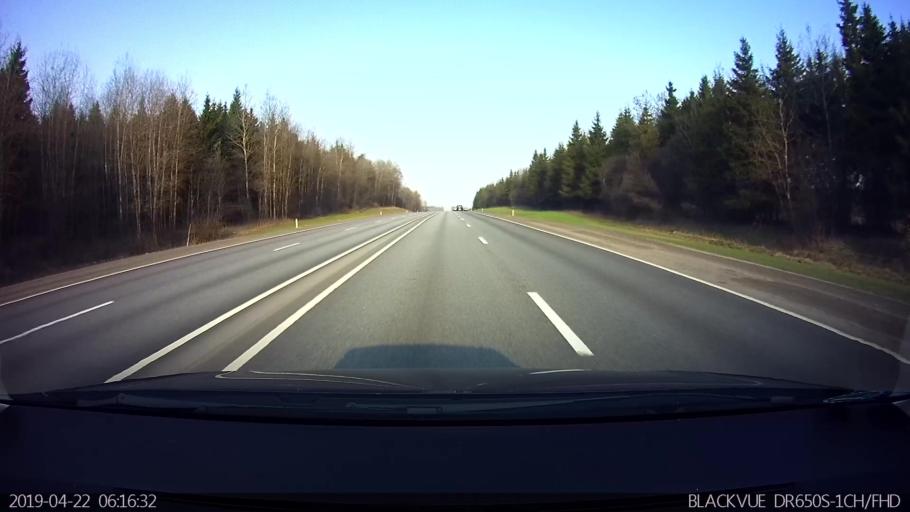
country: RU
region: Moskovskaya
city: Mozhaysk
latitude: 55.4604
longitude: 36.0167
